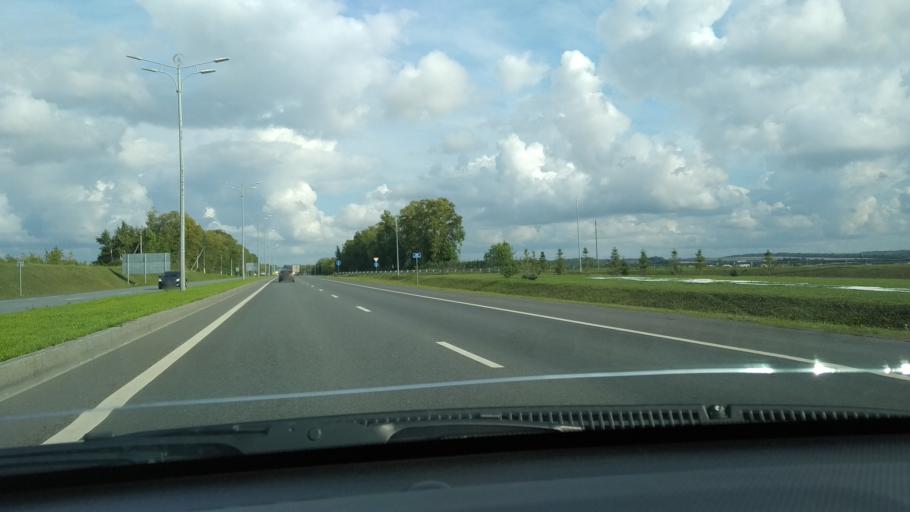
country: RU
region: Tatarstan
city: Stolbishchi
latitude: 55.6614
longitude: 49.2976
